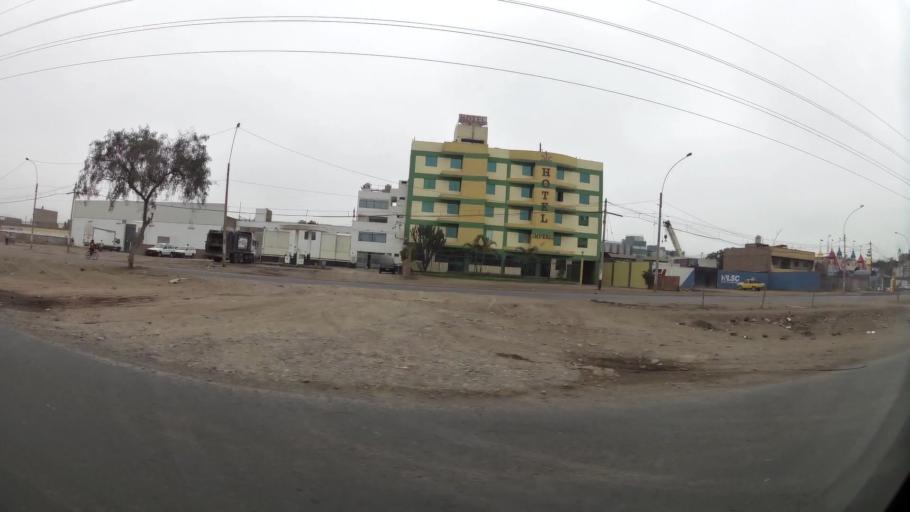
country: PE
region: Lima
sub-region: Lima
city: Urb. Santo Domingo
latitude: -11.9278
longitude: -77.0643
